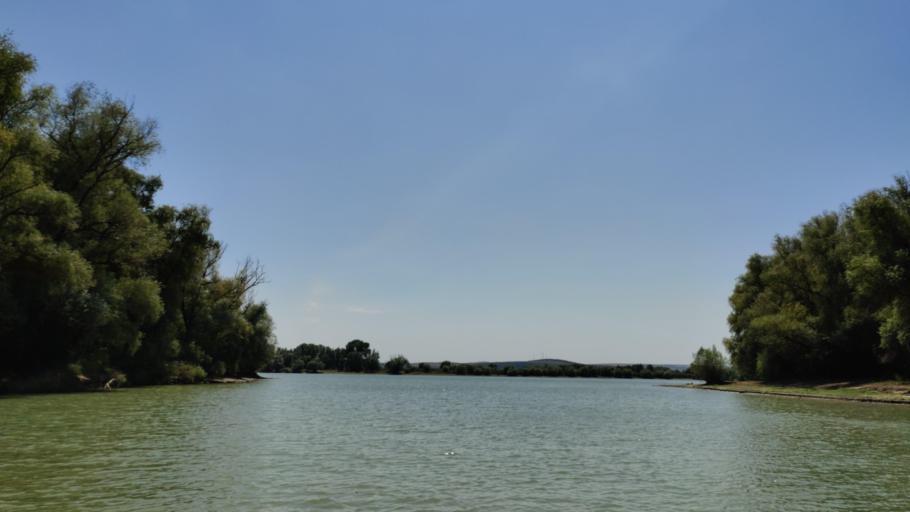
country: RO
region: Tulcea
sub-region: Municipiul Tulcea
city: Tulcea
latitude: 45.2056
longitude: 28.8529
